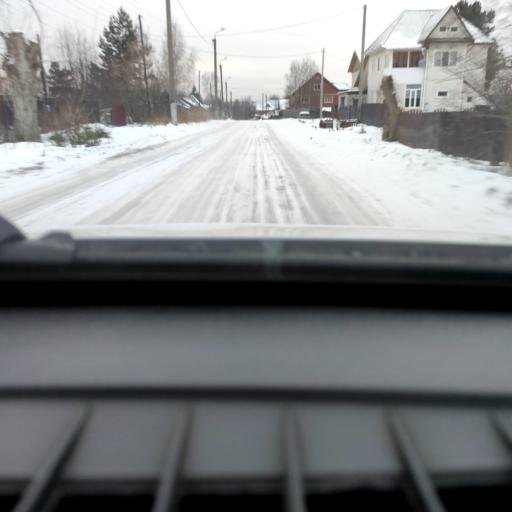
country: RU
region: Perm
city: Perm
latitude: 58.1016
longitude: 56.3689
